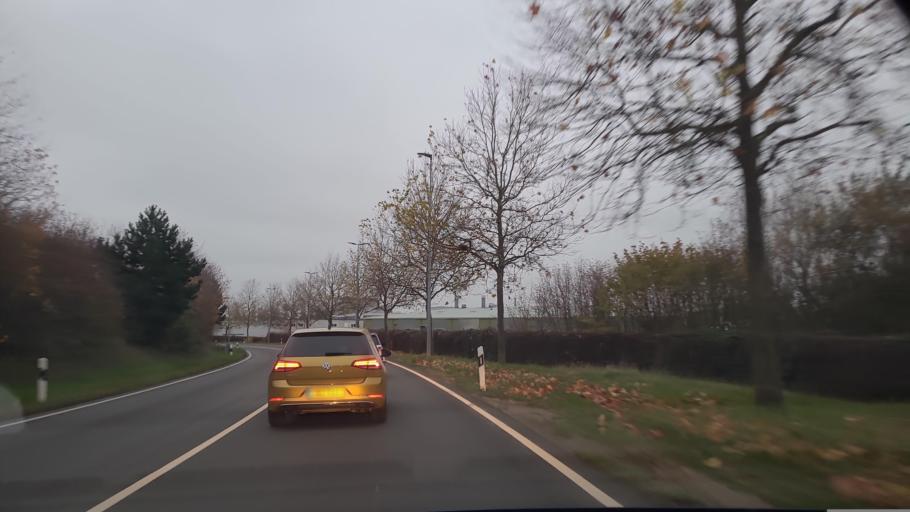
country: LU
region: Luxembourg
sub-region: Canton de Luxembourg
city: Bertrange
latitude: 49.6162
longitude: 6.0545
